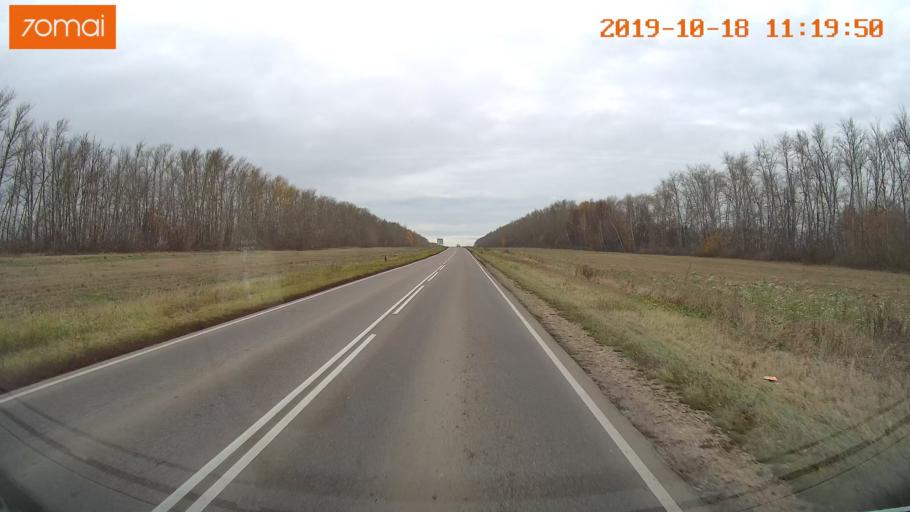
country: RU
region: Tula
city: Kimovsk
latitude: 54.0514
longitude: 38.5558
